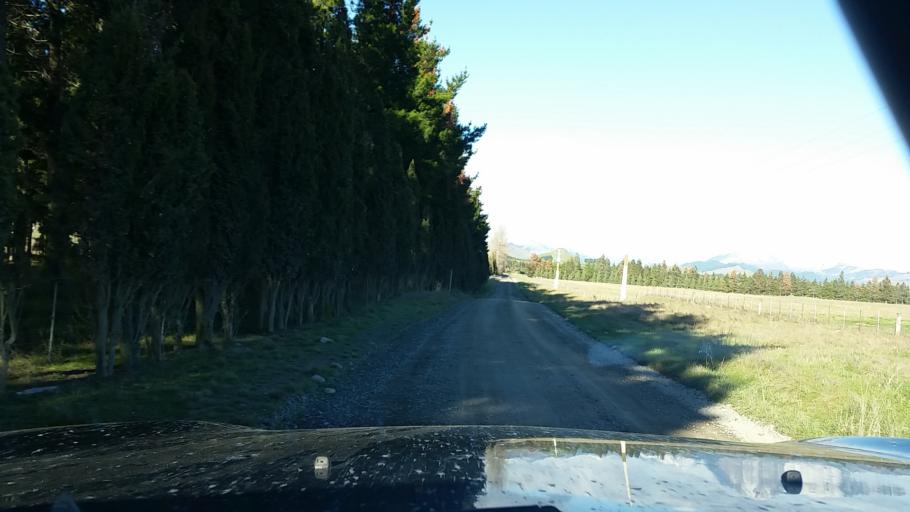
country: NZ
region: Marlborough
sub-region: Marlborough District
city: Blenheim
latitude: -41.6095
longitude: 173.6897
